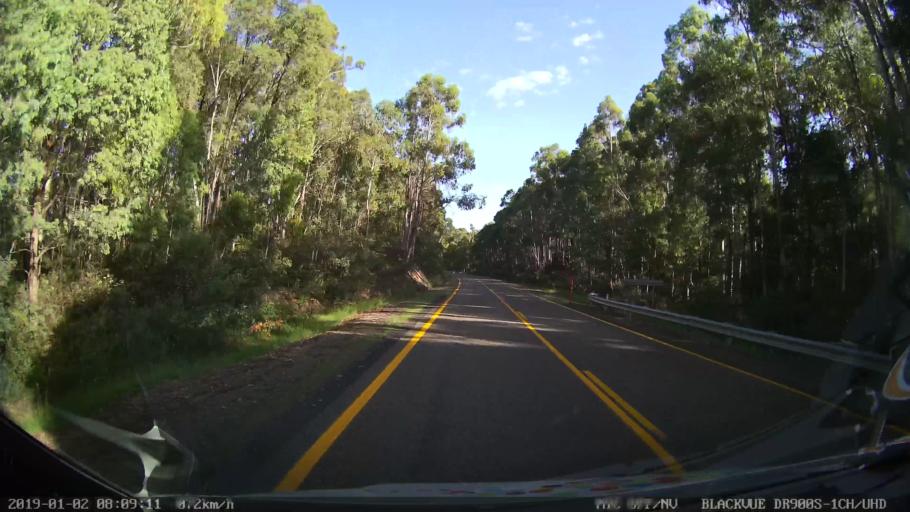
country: AU
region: New South Wales
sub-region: Tumut Shire
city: Tumut
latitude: -35.6095
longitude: 148.3810
